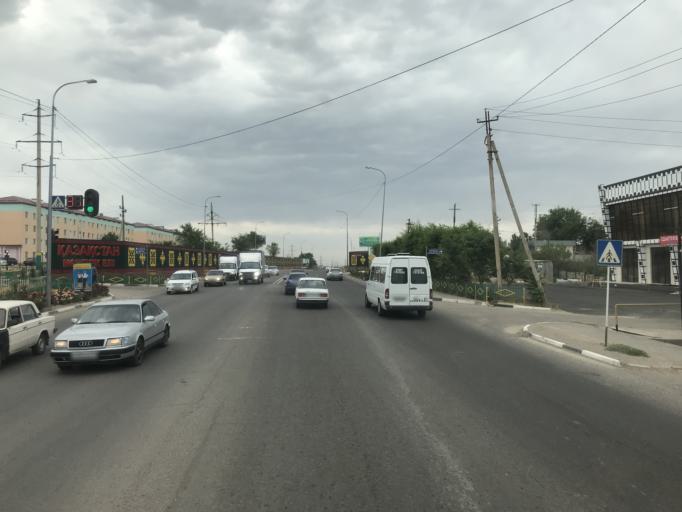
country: KZ
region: Ongtustik Qazaqstan
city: Saryaghash
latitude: 41.4656
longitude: 69.1660
